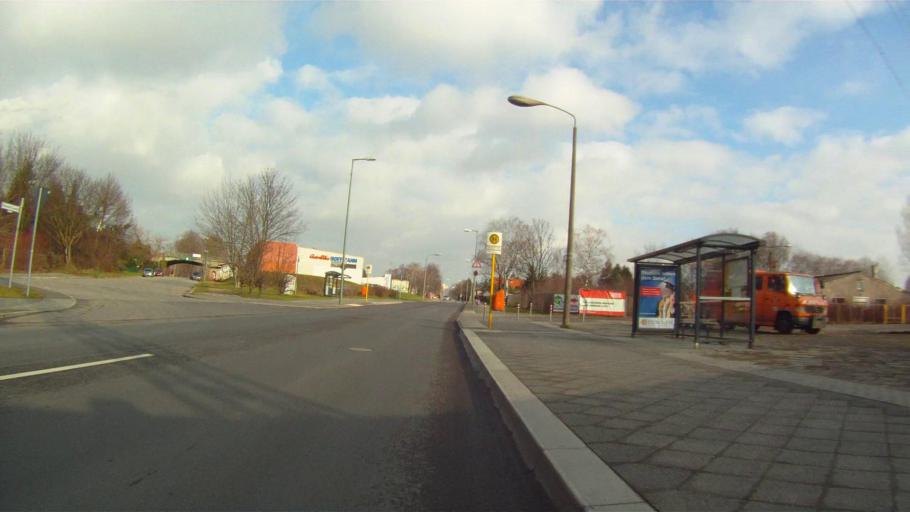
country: DE
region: Berlin
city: Friedrichsfelde
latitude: 52.5142
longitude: 13.5251
